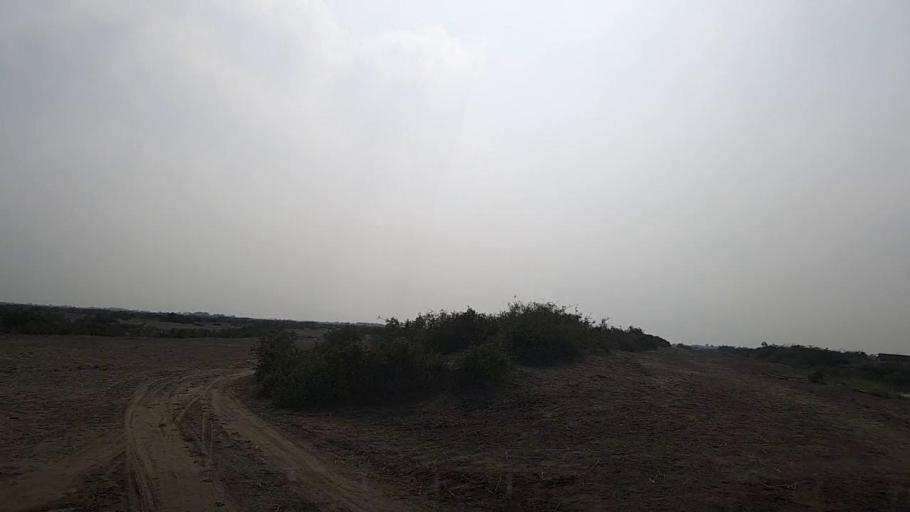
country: PK
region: Sindh
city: Gharo
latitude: 24.6743
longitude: 67.6452
